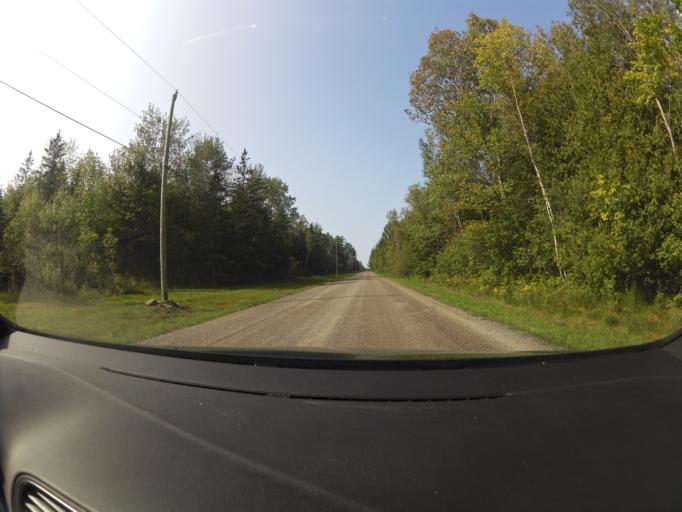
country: CA
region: Ontario
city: Carleton Place
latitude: 45.3108
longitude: -76.1331
